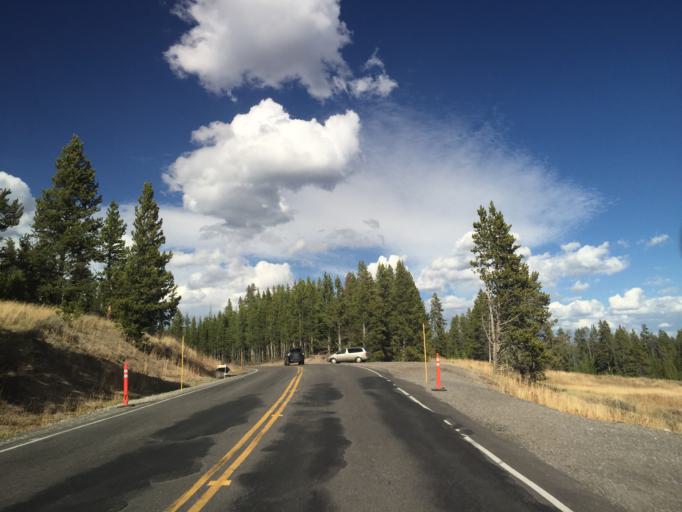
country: US
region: Montana
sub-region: Gallatin County
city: West Yellowstone
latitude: 44.7120
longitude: -110.5047
